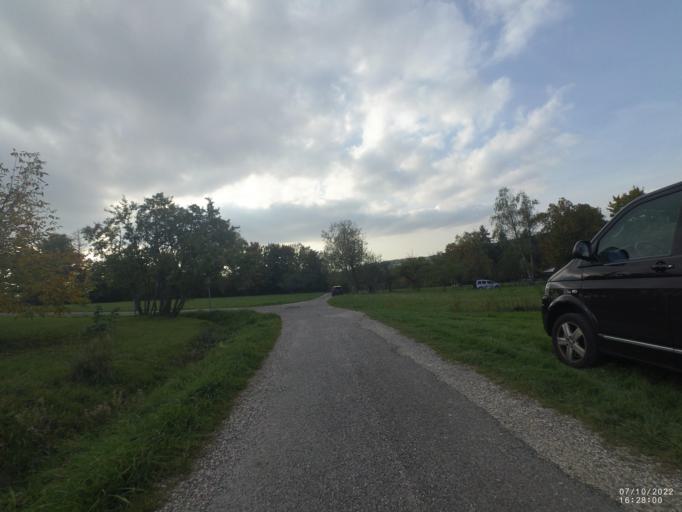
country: DE
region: Baden-Wuerttemberg
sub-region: Regierungsbezirk Stuttgart
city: Eislingen
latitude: 48.7078
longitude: 9.7192
